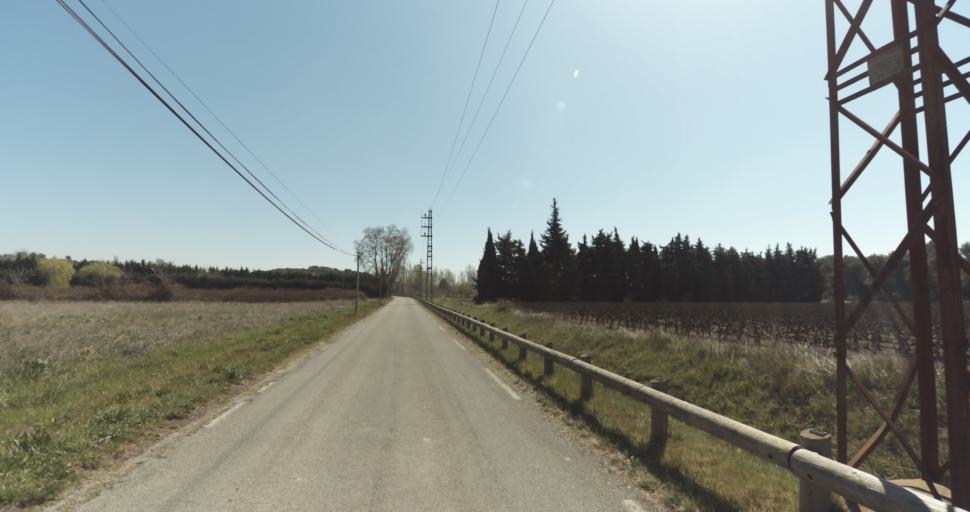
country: FR
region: Provence-Alpes-Cote d'Azur
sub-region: Departement des Bouches-du-Rhone
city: Pelissanne
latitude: 43.6182
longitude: 5.1620
